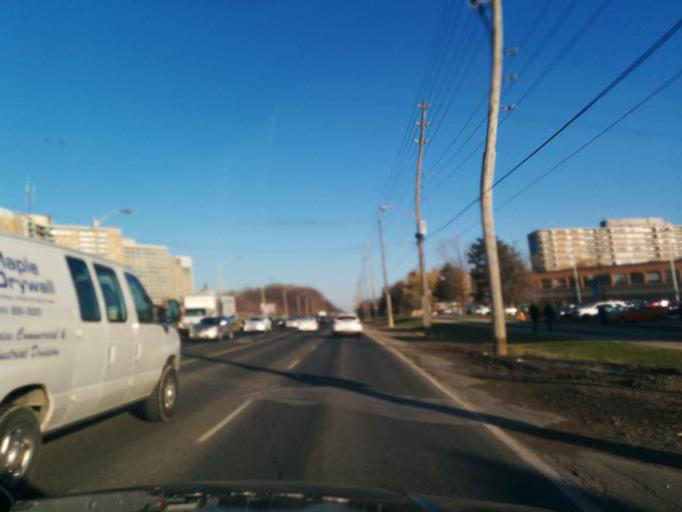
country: CA
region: Ontario
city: Etobicoke
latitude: 43.6755
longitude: -79.5577
